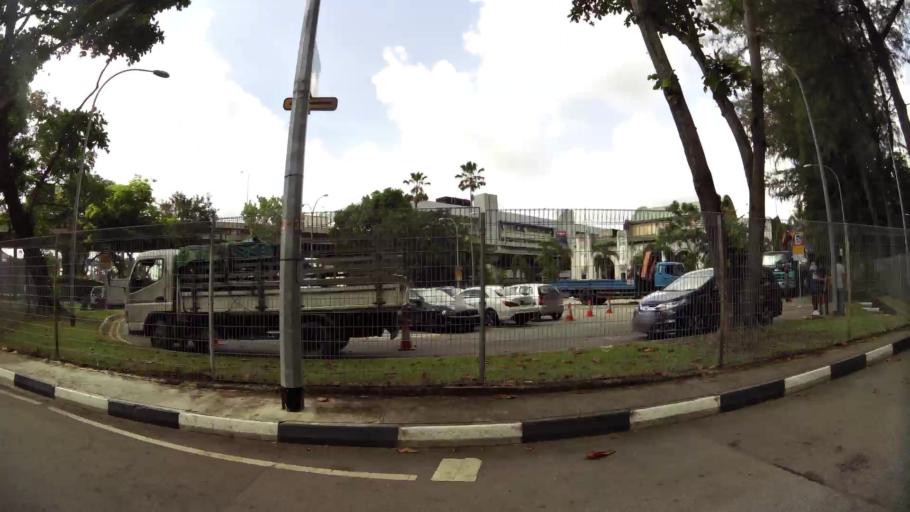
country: SG
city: Singapore
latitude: 1.2733
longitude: 103.8397
